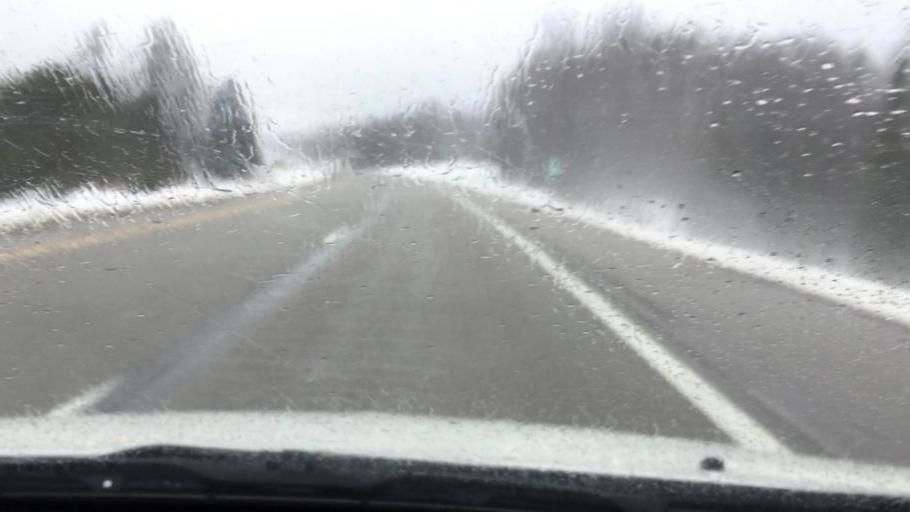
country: US
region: Michigan
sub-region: Wexford County
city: Cadillac
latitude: 44.1448
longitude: -85.4668
